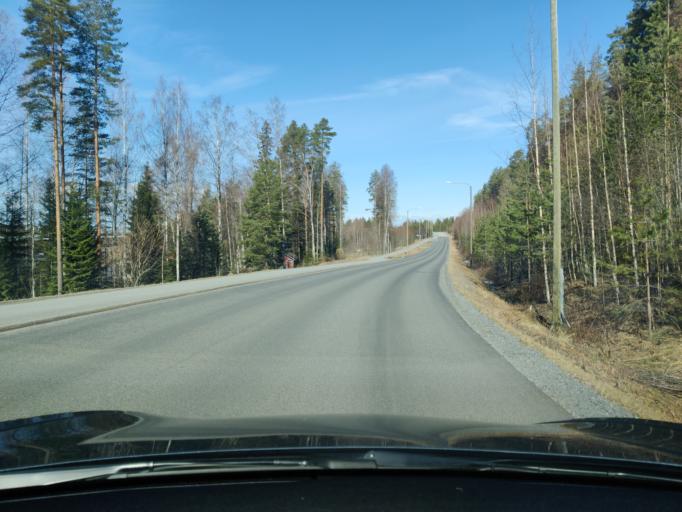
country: FI
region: Northern Savo
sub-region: Kuopio
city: Vehmersalmi
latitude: 62.7670
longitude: 28.0128
